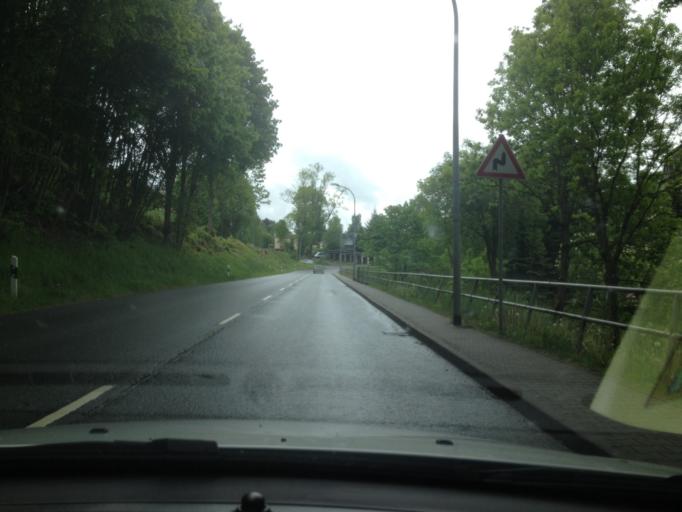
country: DE
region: Saxony
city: Annaberg-Buchholz
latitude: 50.5618
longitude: 12.9991
